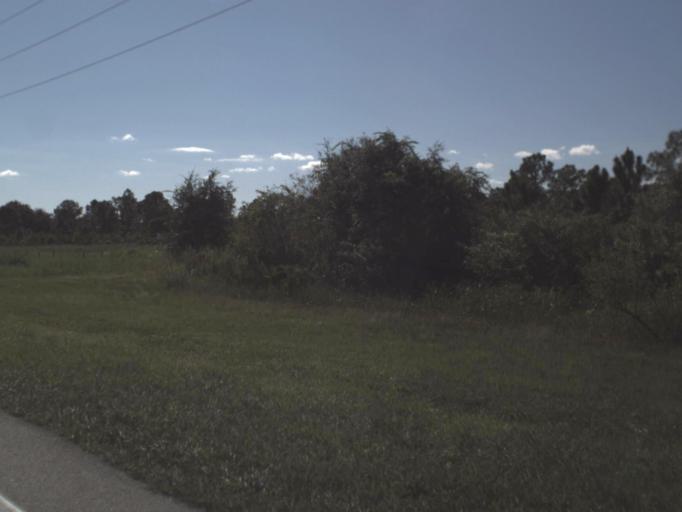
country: US
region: Florida
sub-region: Lee County
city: Gateway
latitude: 26.5718
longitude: -81.6909
